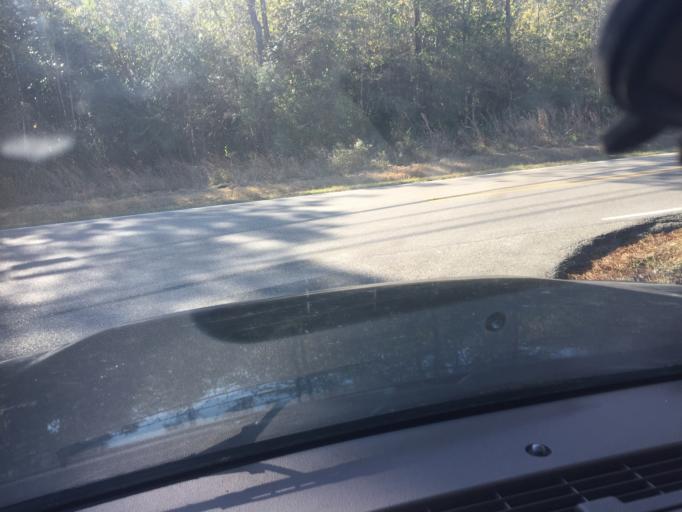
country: US
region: Louisiana
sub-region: Saint Tammany Parish
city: Slidell
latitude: 30.3104
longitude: -89.7366
